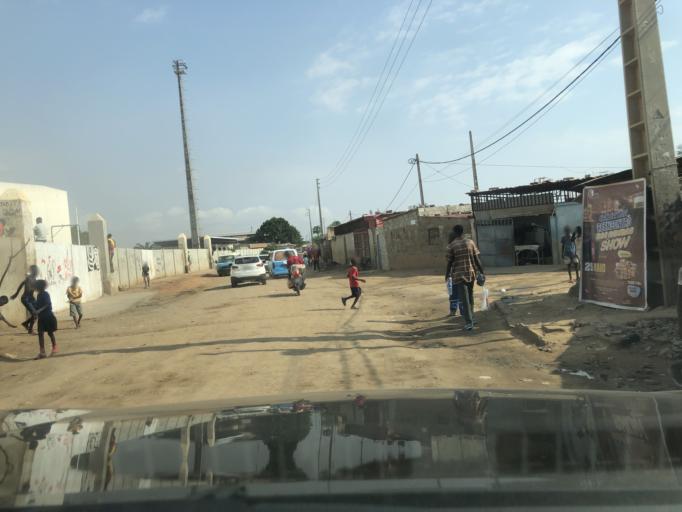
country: AO
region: Luanda
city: Luanda
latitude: -8.8546
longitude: 13.2540
